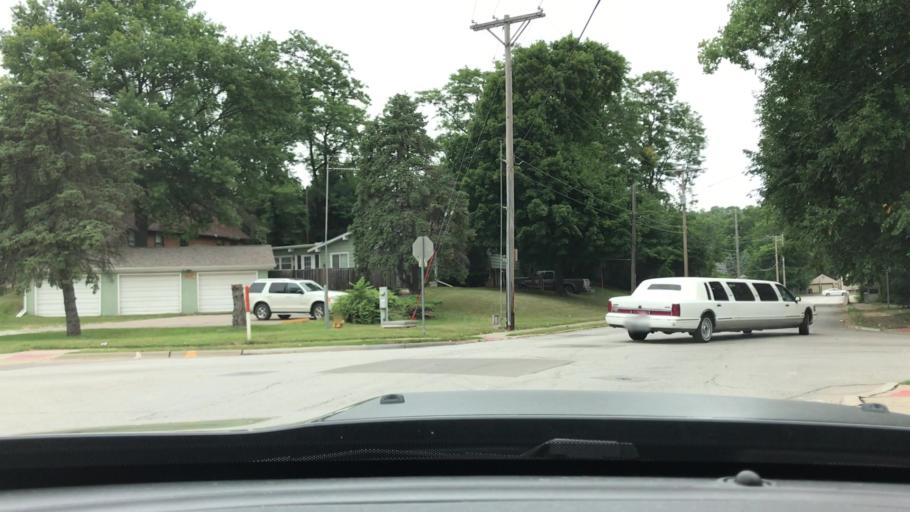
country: US
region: Illinois
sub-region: Rock Island County
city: Rock Island
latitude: 41.5170
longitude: -90.6222
